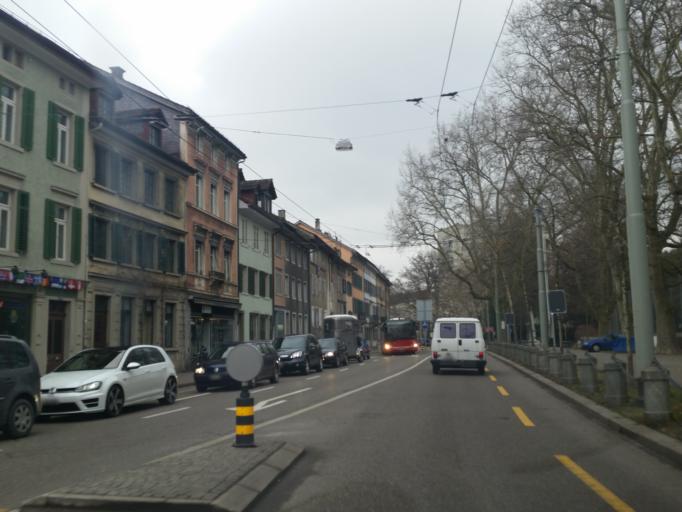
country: CH
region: Zurich
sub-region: Bezirk Winterthur
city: Stadt Winterthur (Kreis 1) / Altstadt
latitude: 47.4987
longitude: 8.7330
